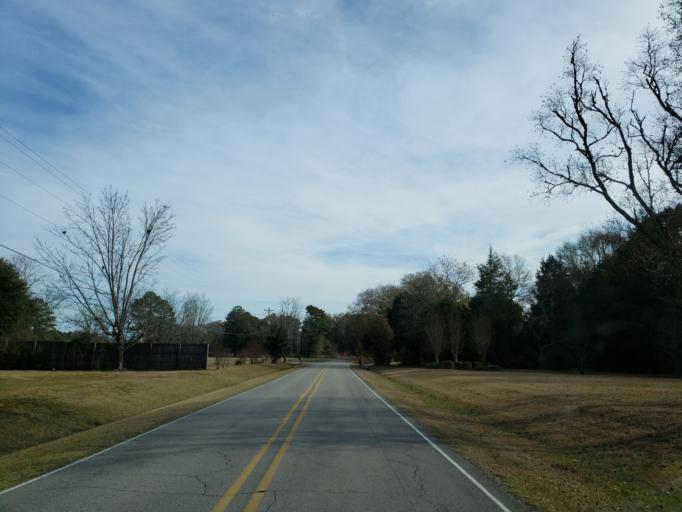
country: US
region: Mississippi
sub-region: Forrest County
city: Rawls Springs
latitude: 31.3905
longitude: -89.3807
